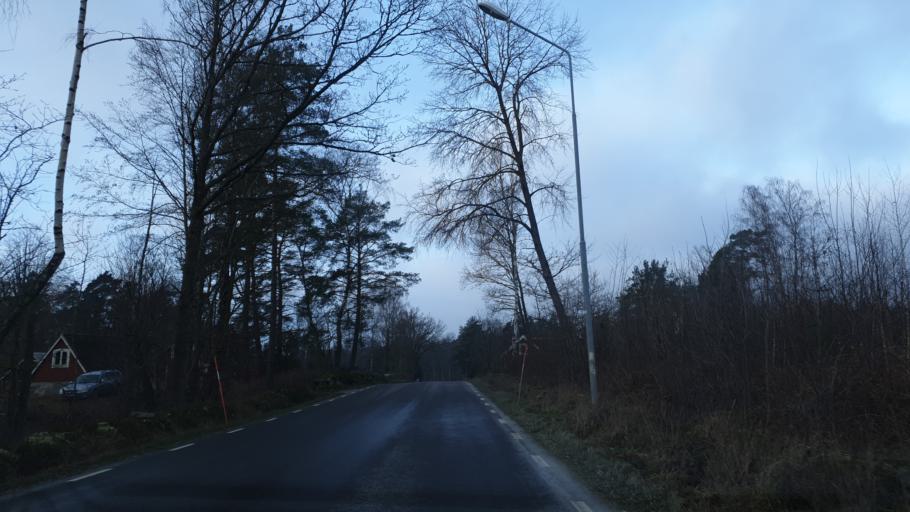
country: SE
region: Blekinge
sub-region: Karlshamns Kommun
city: Morrum
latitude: 56.1730
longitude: 14.7356
